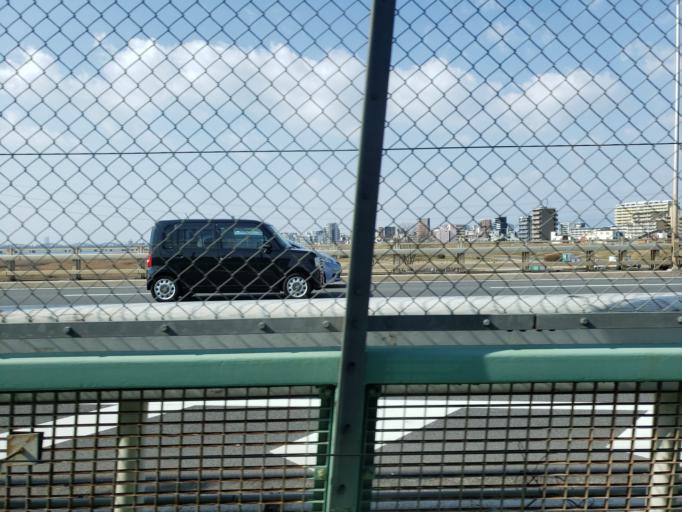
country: JP
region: Osaka
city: Osaka-shi
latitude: 34.7220
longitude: 135.4991
